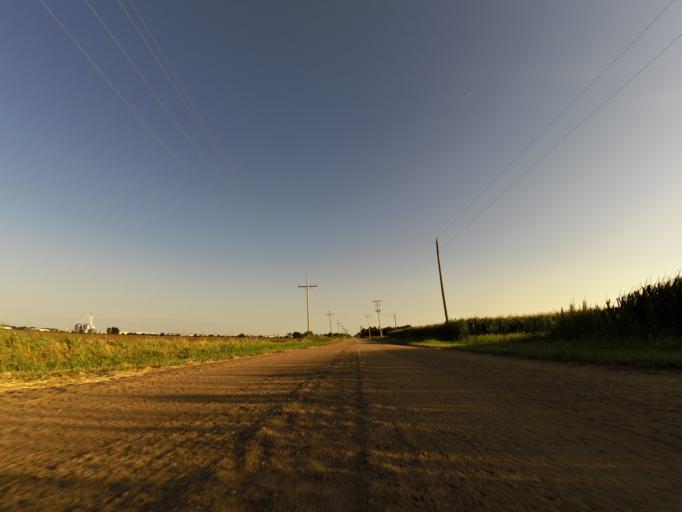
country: US
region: Kansas
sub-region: Reno County
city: South Hutchinson
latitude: 38.0039
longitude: -98.0319
